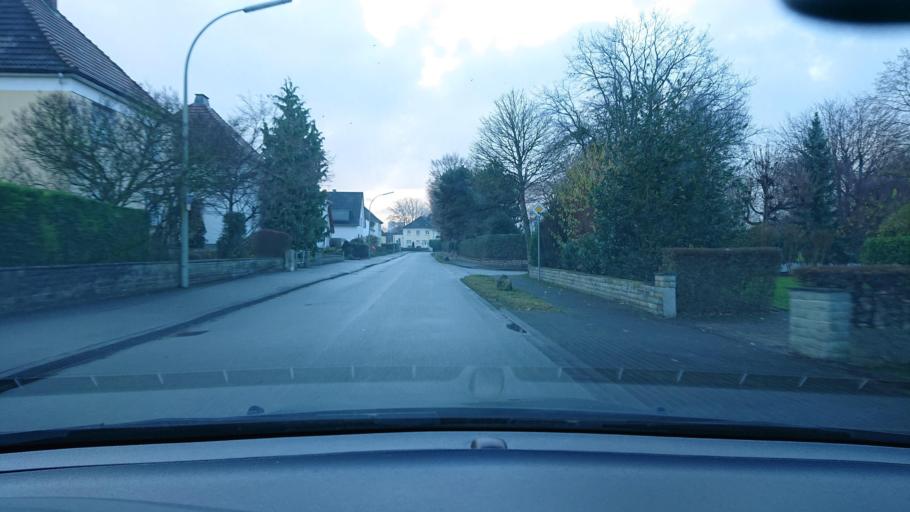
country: DE
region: North Rhine-Westphalia
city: Erwitte
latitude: 51.6174
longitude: 8.3319
